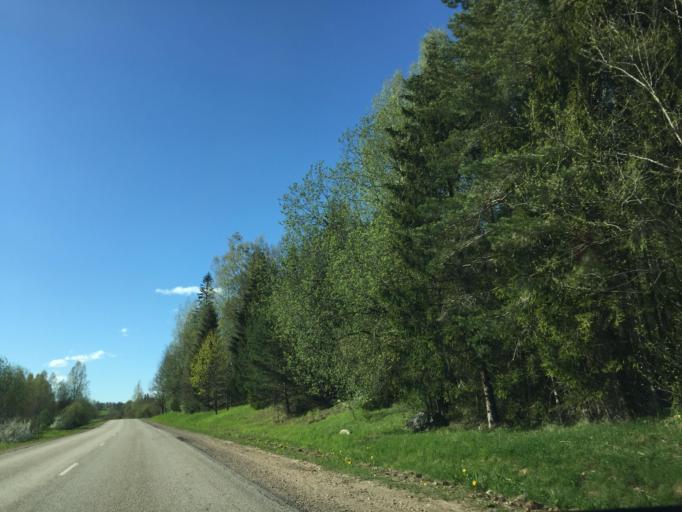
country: LV
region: Madonas Rajons
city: Madona
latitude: 56.8120
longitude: 26.0156
